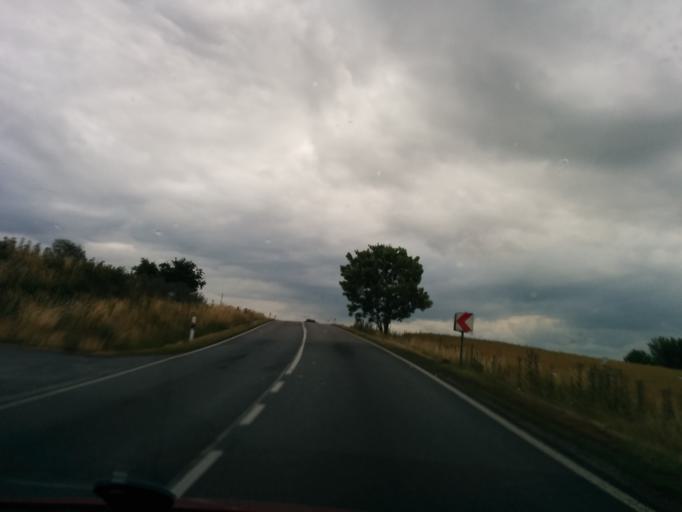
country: DE
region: Thuringia
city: Sondershausen
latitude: 51.3200
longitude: 10.8476
